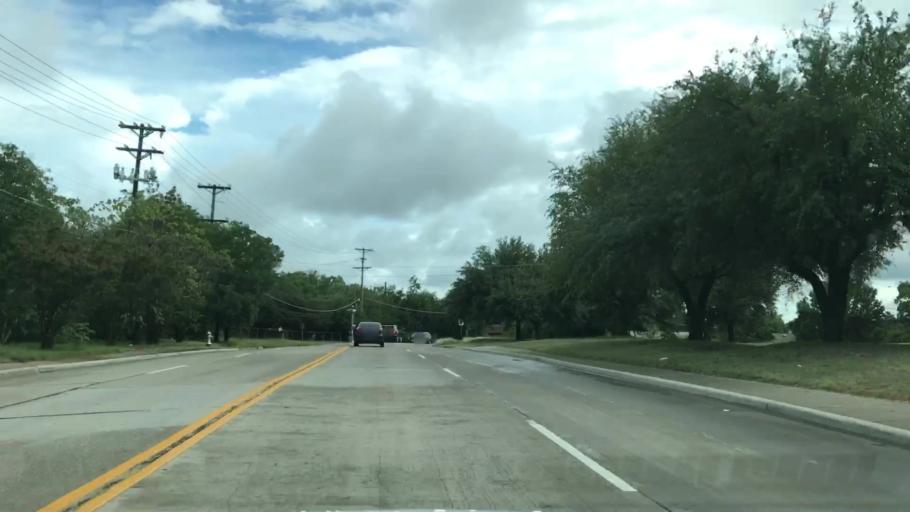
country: US
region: Texas
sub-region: Dallas County
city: Irving
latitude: 32.8527
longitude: -96.9752
